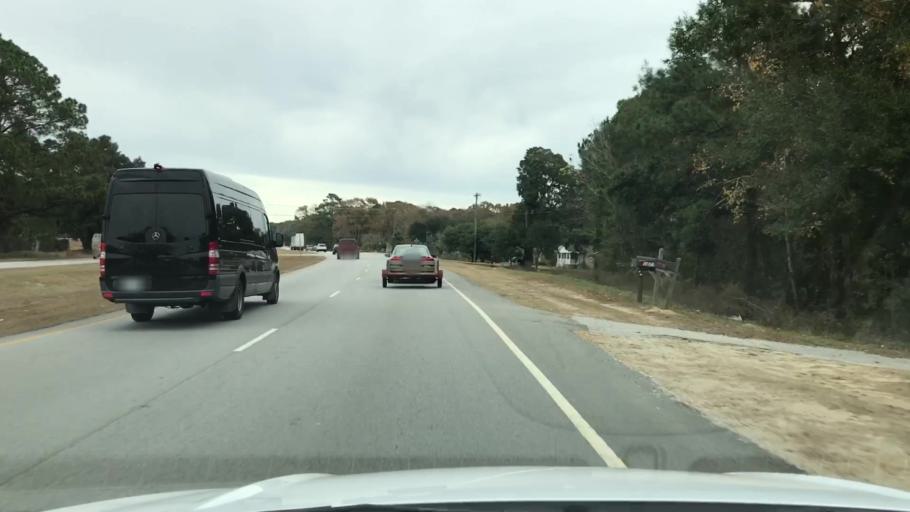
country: US
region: South Carolina
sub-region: Charleston County
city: Isle of Palms
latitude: 32.8841
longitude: -79.7498
